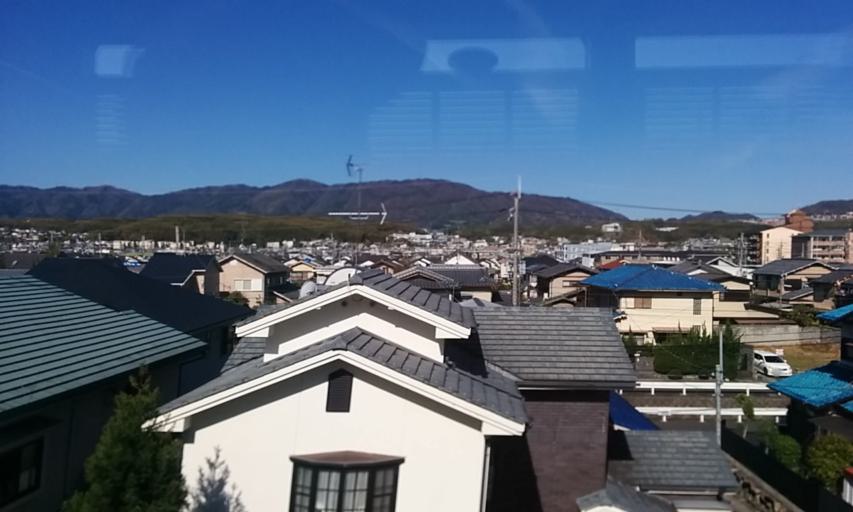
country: JP
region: Kyoto
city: Muko
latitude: 34.9722
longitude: 135.7030
